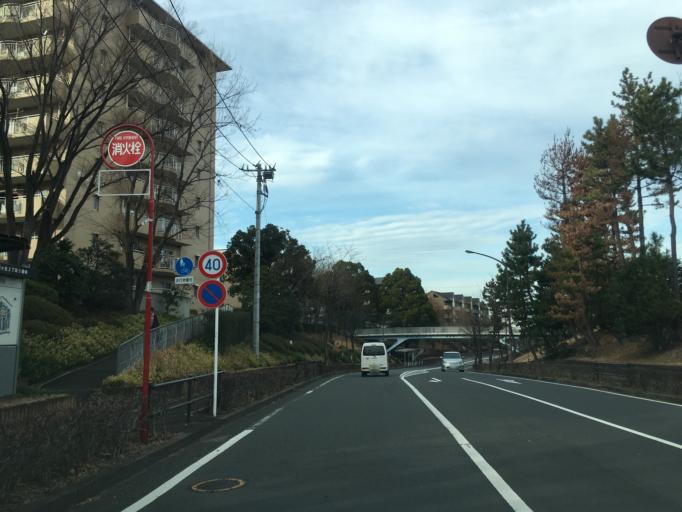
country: JP
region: Tokyo
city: Hino
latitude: 35.6170
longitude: 139.4374
